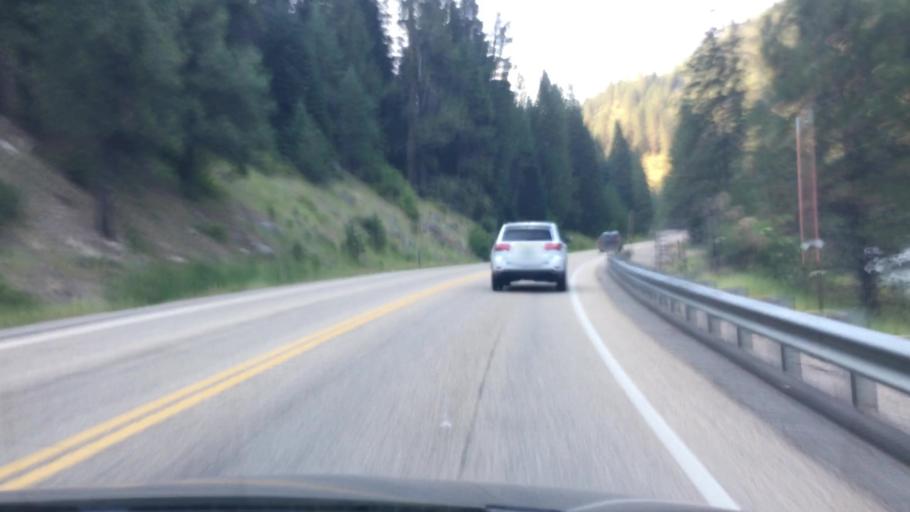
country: US
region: Idaho
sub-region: Valley County
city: Cascade
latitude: 44.1905
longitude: -116.1149
